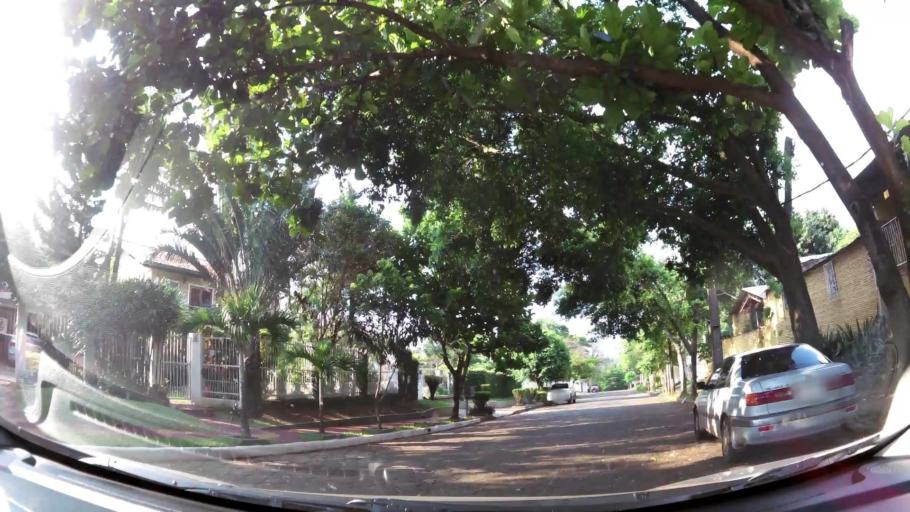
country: PY
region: Alto Parana
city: Presidente Franco
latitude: -25.5312
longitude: -54.6302
